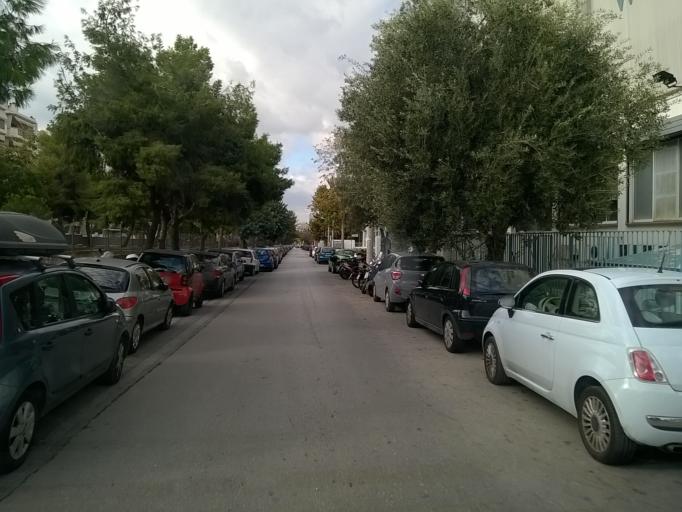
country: GR
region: Attica
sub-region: Nomarchia Athinas
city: Tavros
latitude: 37.9588
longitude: 23.6913
